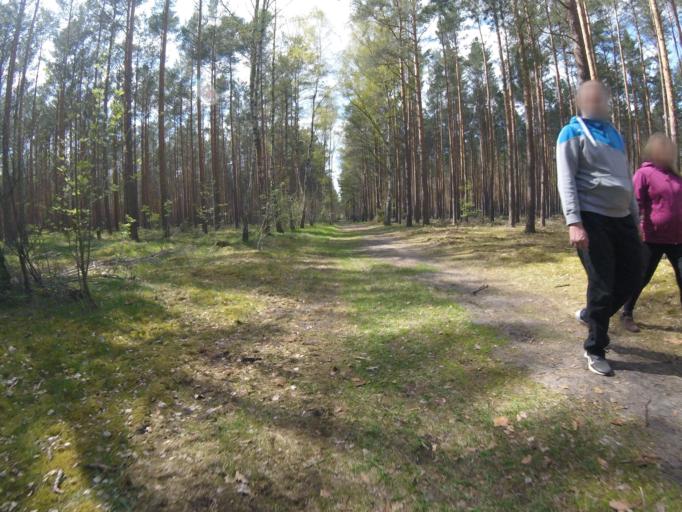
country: DE
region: Brandenburg
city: Gross Koris
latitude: 52.1978
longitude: 13.7037
